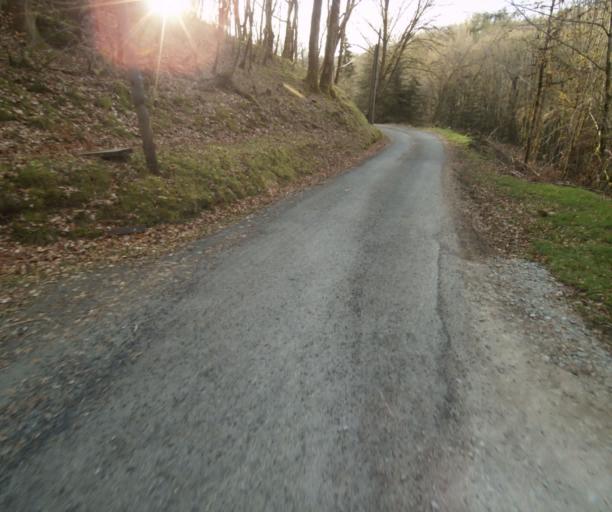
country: FR
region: Limousin
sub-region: Departement de la Correze
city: Correze
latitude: 45.3552
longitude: 1.8265
